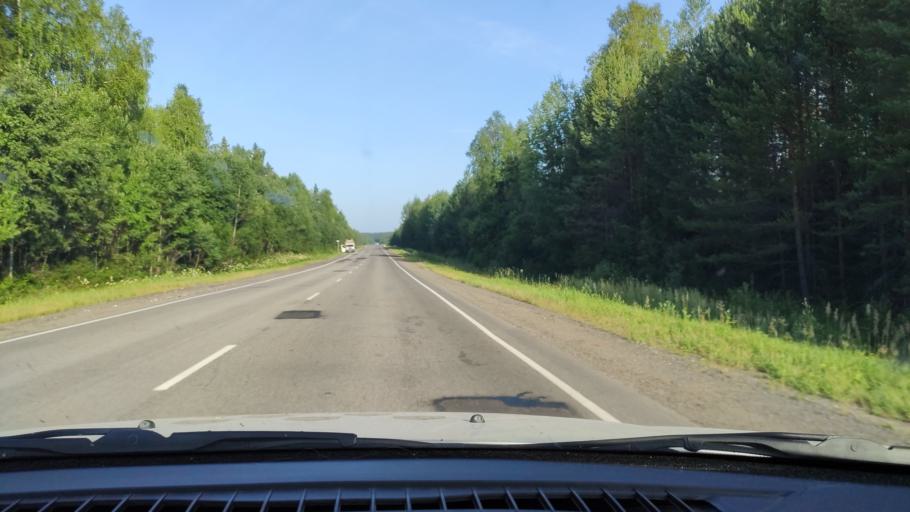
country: RU
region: Kirov
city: Dubrovka
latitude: 58.9027
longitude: 51.2853
